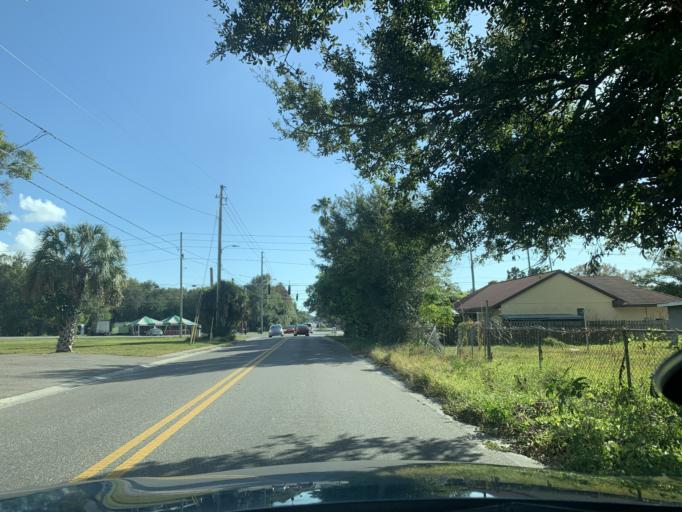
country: US
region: Florida
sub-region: Pinellas County
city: Belleair
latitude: 27.9397
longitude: -82.7915
